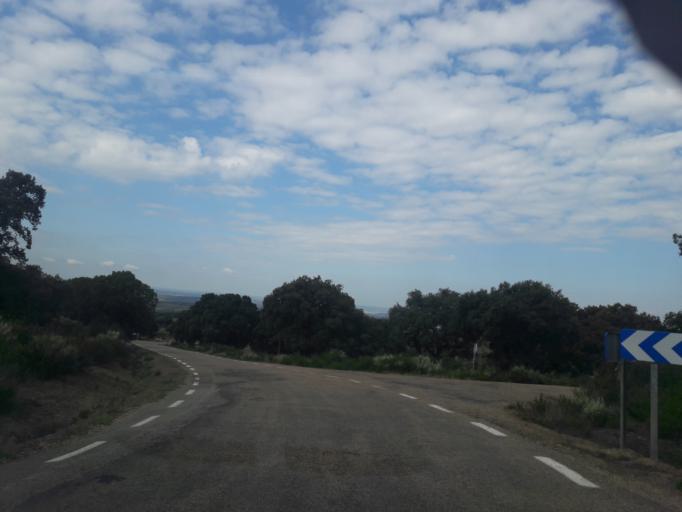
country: ES
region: Castille and Leon
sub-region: Provincia de Salamanca
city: Serradilla del Arroyo
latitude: 40.5425
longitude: -6.4040
